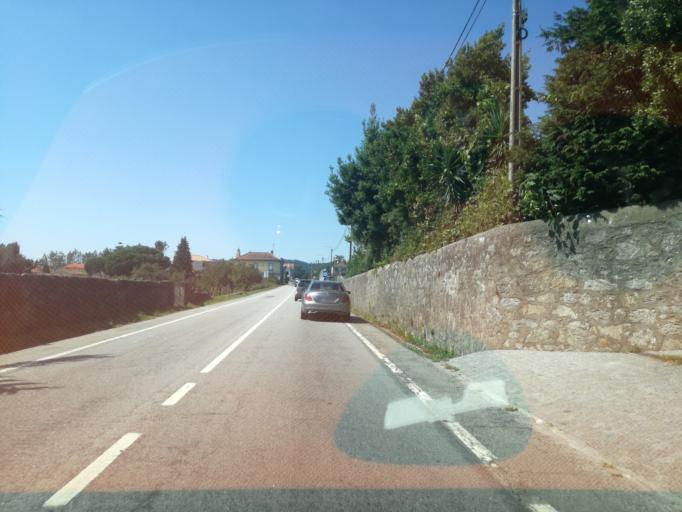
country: PT
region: Viana do Castelo
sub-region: Viana do Castelo
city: Darque
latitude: 41.6586
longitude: -8.7810
